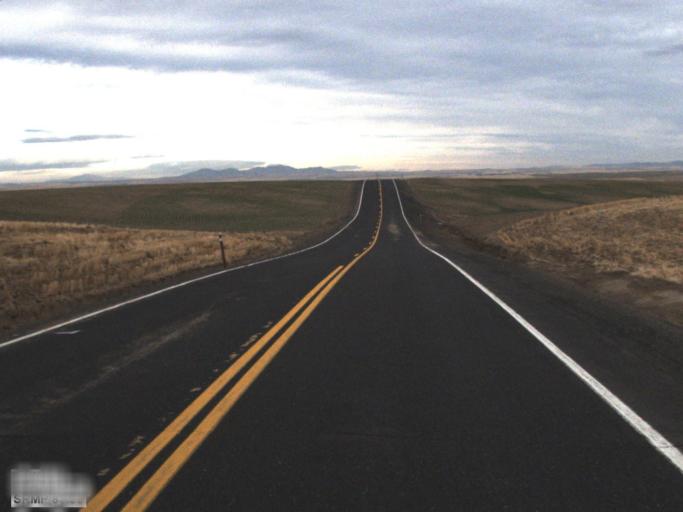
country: US
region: Washington
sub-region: Okanogan County
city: Coulee Dam
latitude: 47.6482
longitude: -118.7211
